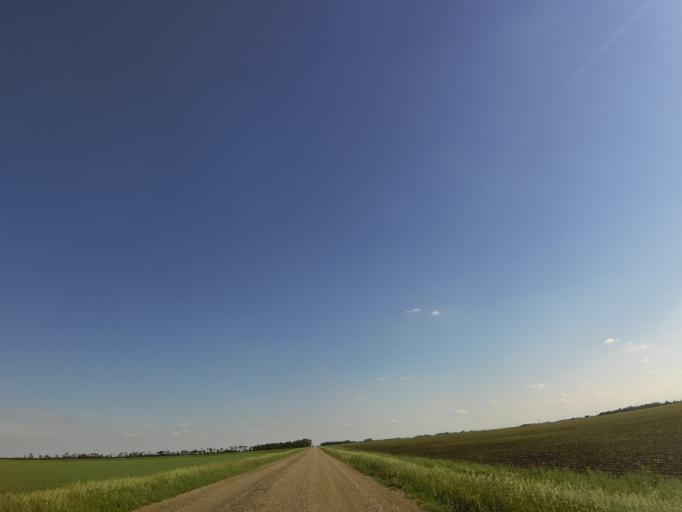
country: US
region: North Dakota
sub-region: Walsh County
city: Grafton
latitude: 48.4016
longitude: -97.2557
